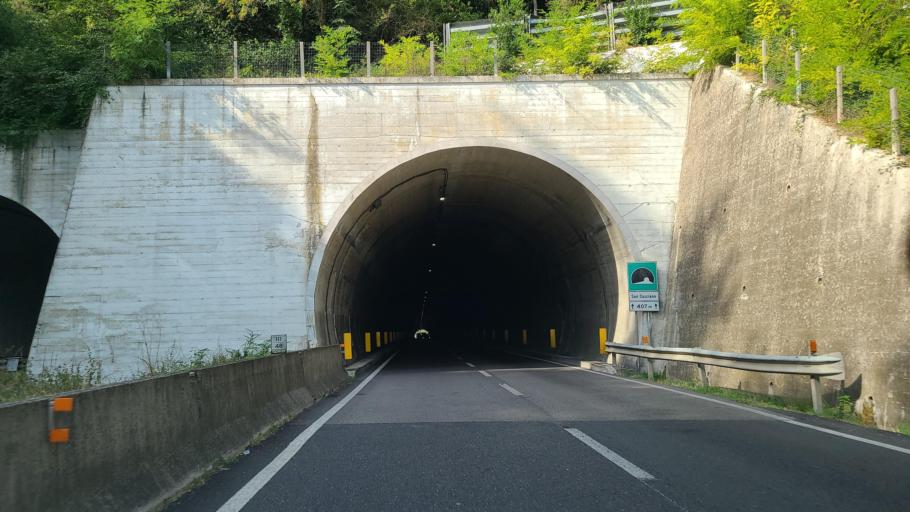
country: IT
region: Tuscany
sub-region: Province of Florence
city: San Casciano in Val di Pesa
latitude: 43.6557
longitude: 11.1958
